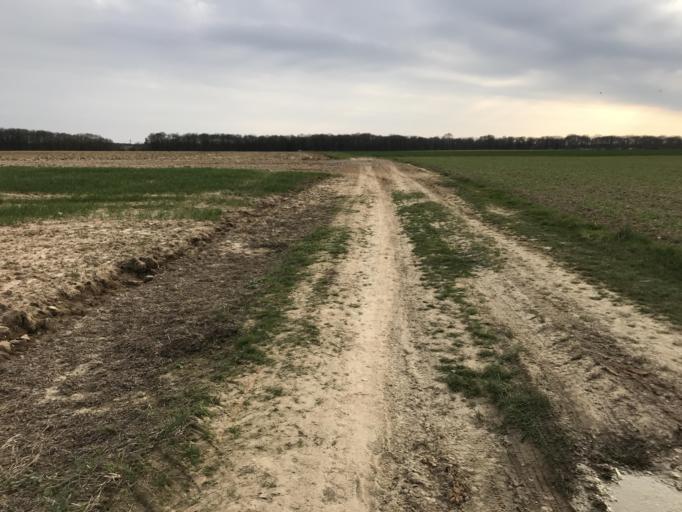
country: FR
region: Ile-de-France
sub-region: Departement de l'Essonne
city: Les Molieres
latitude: 48.6568
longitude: 2.0527
